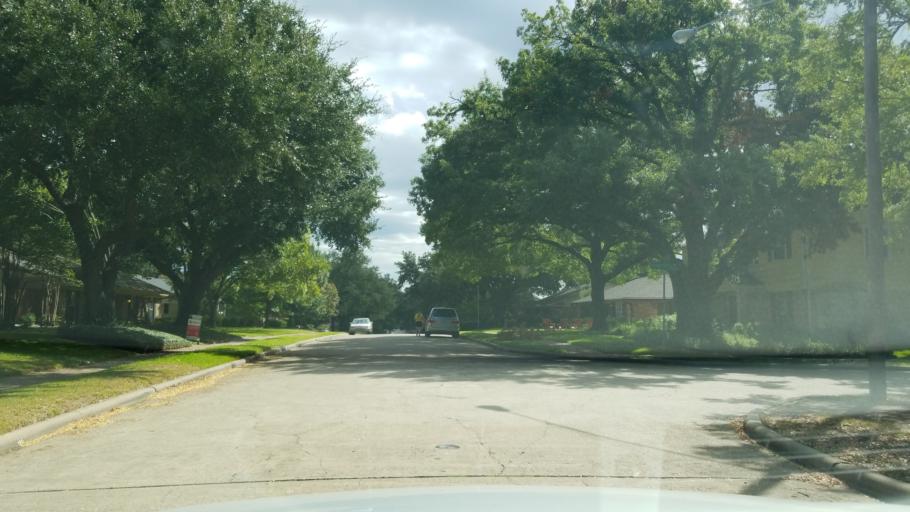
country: US
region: Texas
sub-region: Dallas County
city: Richardson
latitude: 32.9678
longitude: -96.7762
